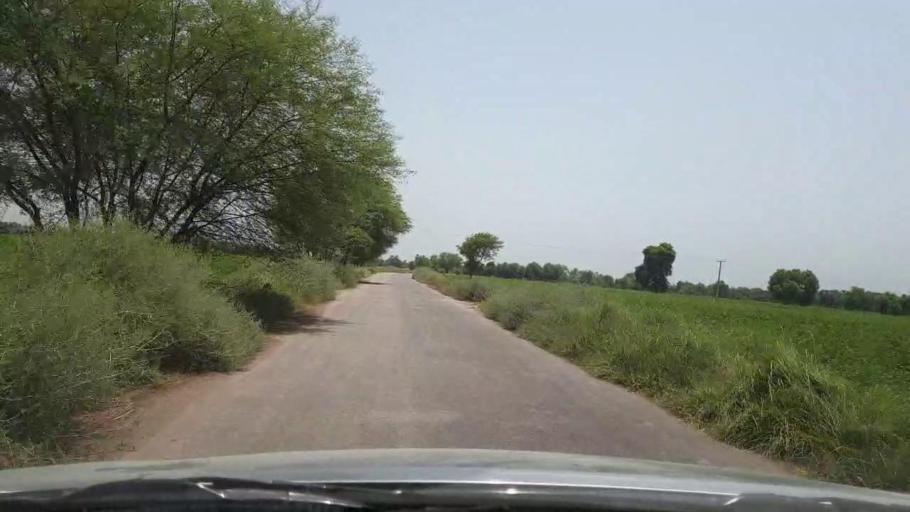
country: PK
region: Sindh
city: Pano Aqil
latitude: 27.8817
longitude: 69.1461
